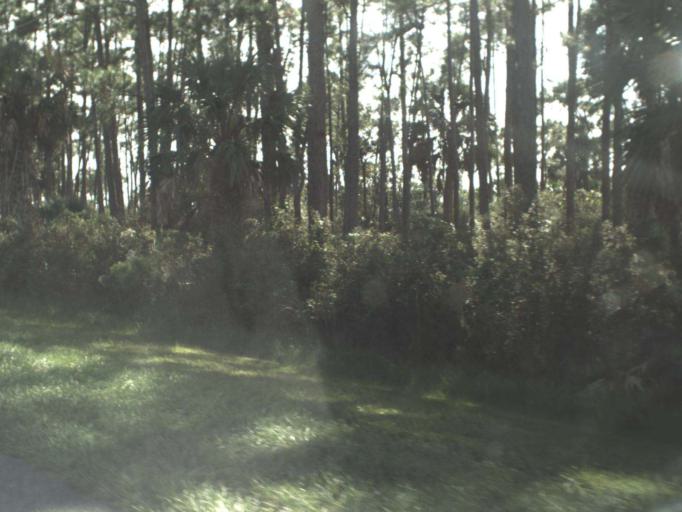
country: US
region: Florida
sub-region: Gulf County
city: Port Saint Joe
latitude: 29.7871
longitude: -85.3013
